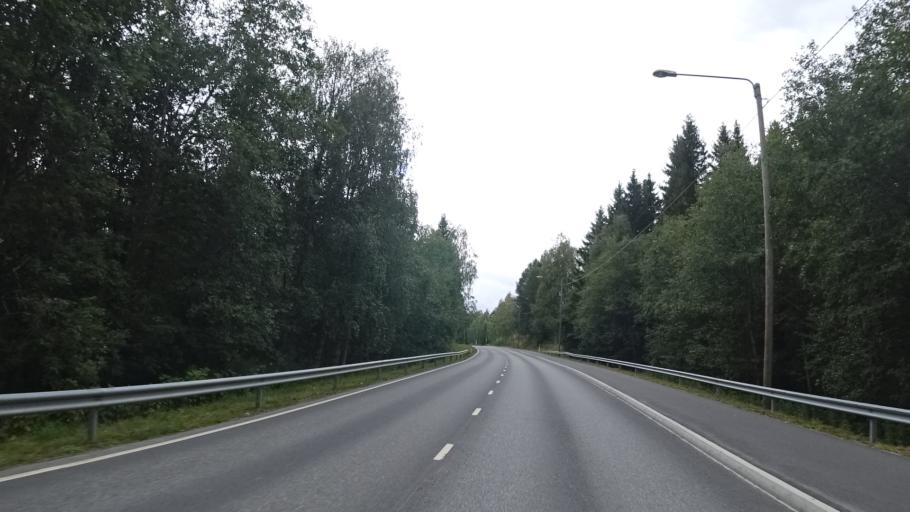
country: FI
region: North Karelia
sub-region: Joensuu
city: Ilomantsi
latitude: 62.6548
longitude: 30.9460
